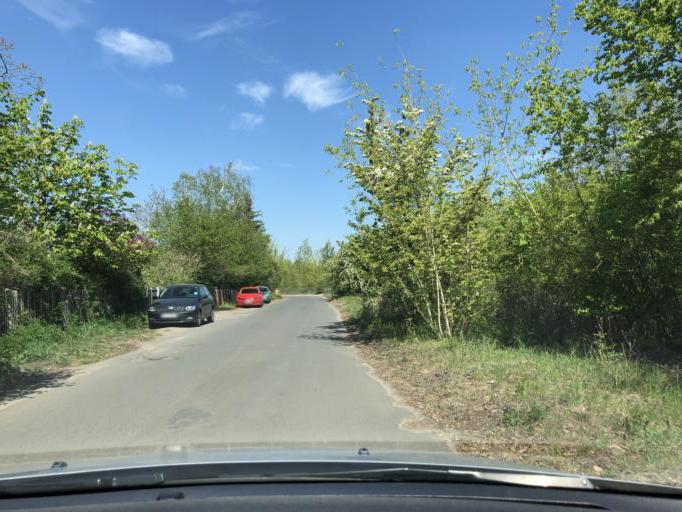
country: DE
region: Saxony-Anhalt
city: Dieskau
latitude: 51.4492
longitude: 11.9992
